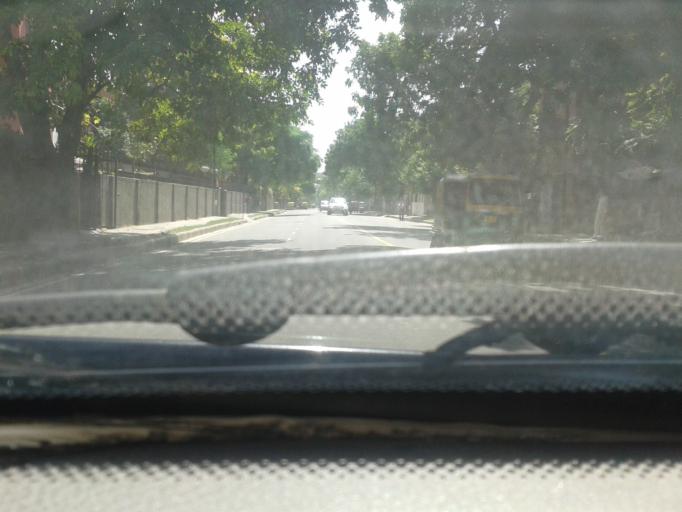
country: IN
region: NCT
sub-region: Central Delhi
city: Karol Bagh
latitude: 28.6306
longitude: 77.2004
